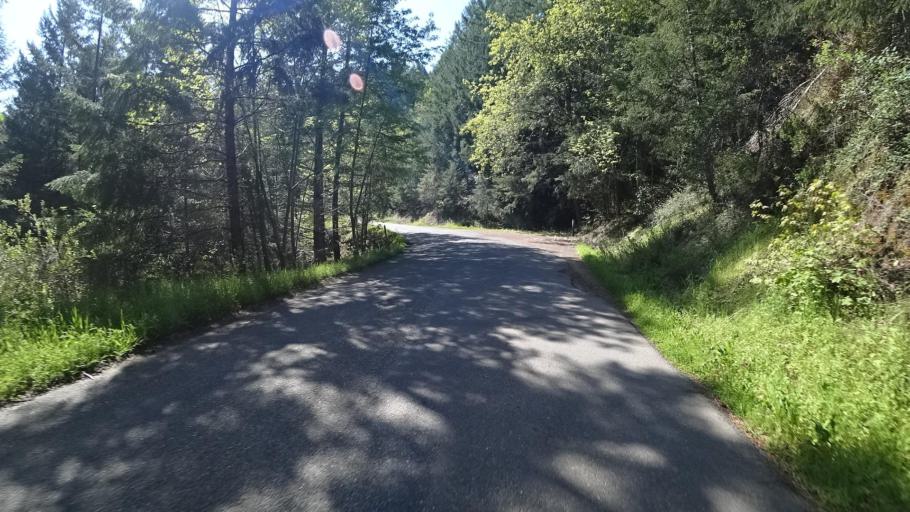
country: US
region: California
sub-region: Humboldt County
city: Redway
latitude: 40.0664
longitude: -123.6502
